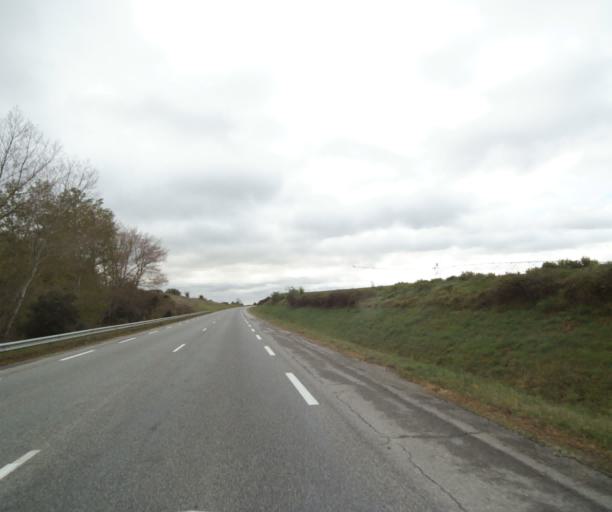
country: FR
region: Midi-Pyrenees
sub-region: Departement de l'Ariege
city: Saverdun
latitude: 43.2358
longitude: 1.5956
